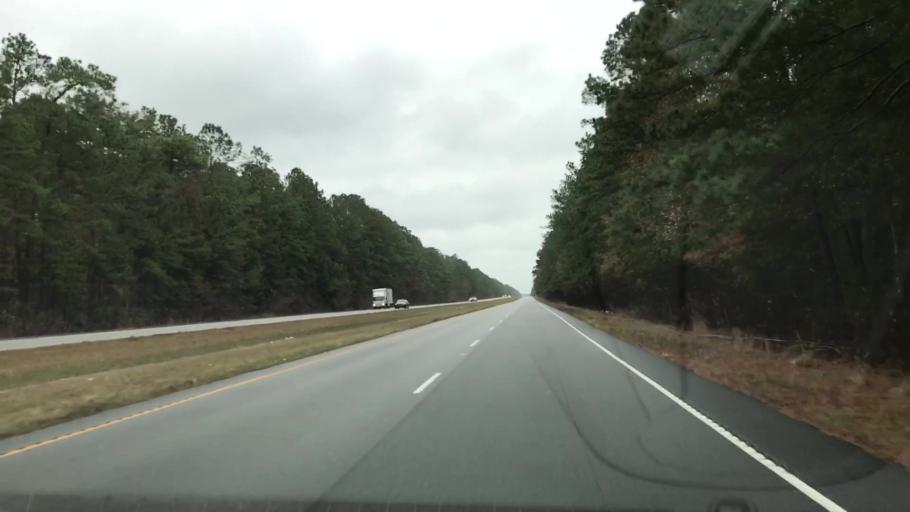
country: US
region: South Carolina
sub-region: Charleston County
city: Awendaw
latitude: 33.1454
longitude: -79.4364
